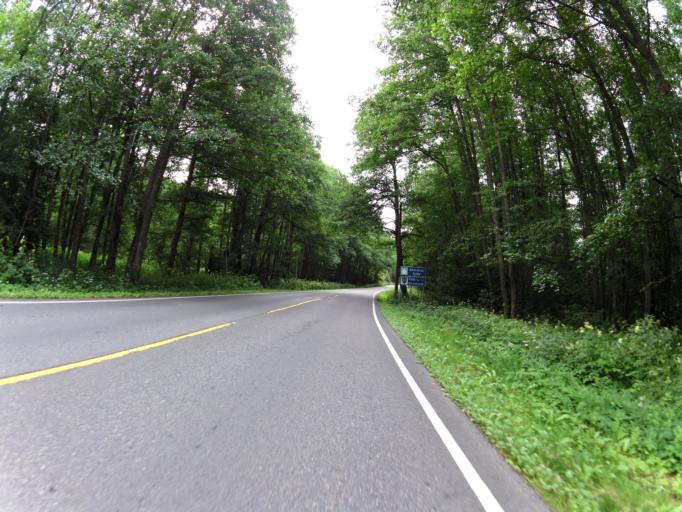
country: NO
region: Akershus
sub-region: Oppegard
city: Kolbotn
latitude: 59.8240
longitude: 10.7724
